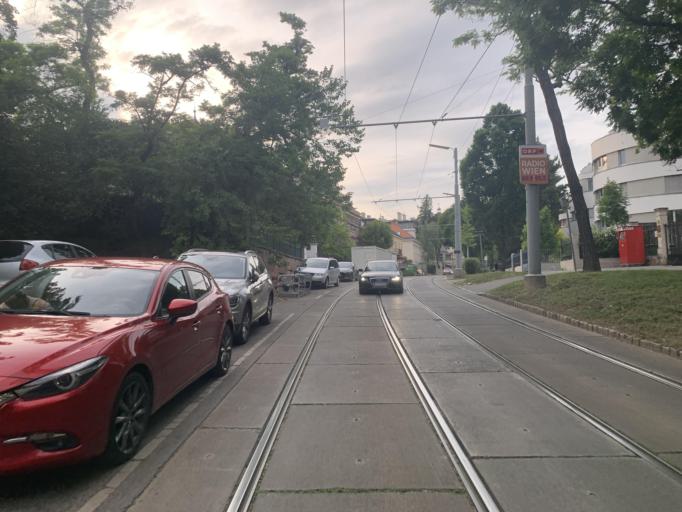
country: AT
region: Vienna
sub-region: Wien Stadt
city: Vienna
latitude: 48.2475
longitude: 16.3555
